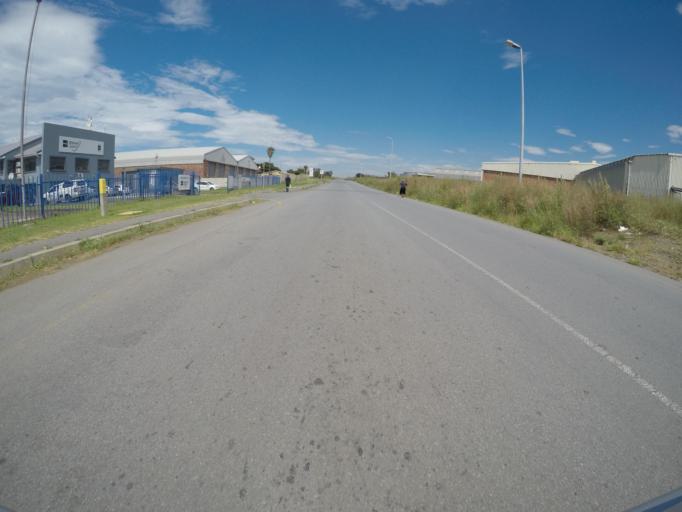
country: ZA
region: Eastern Cape
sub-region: Buffalo City Metropolitan Municipality
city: East London
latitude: -33.0346
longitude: 27.8865
